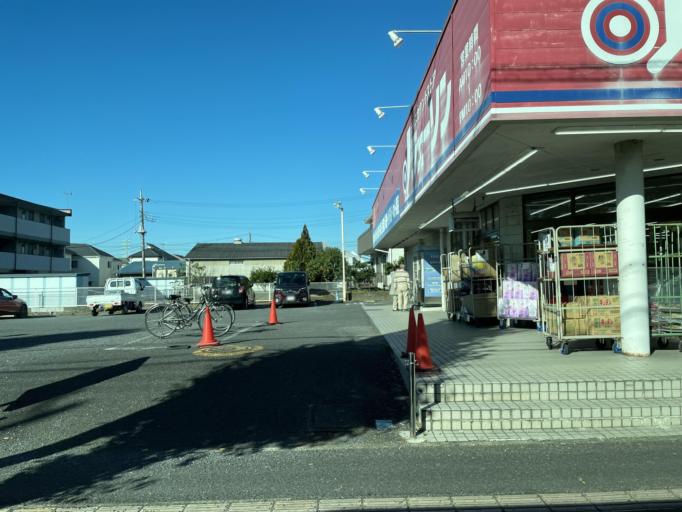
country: JP
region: Saitama
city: Kukichuo
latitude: 36.0638
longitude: 139.6886
